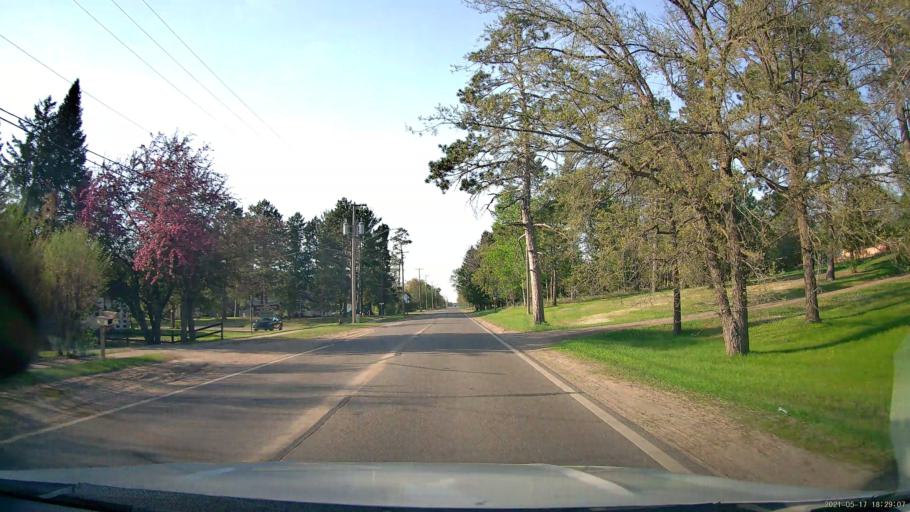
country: US
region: Minnesota
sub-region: Hubbard County
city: Park Rapids
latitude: 46.9228
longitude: -95.0492
